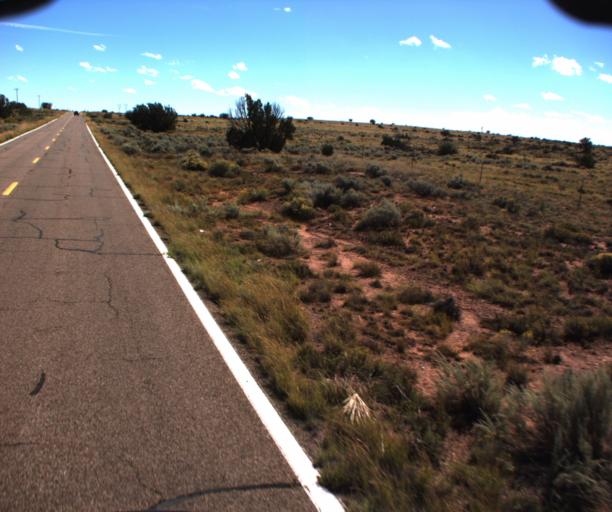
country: US
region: Arizona
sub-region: Apache County
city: Saint Johns
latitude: 34.5733
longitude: -109.6363
